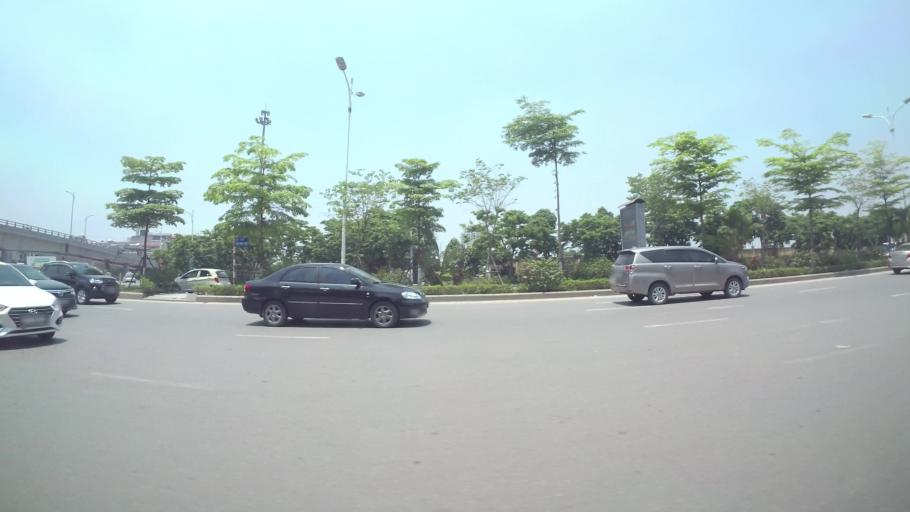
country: VN
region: Ha Noi
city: Trau Quy
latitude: 21.0276
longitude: 105.8970
